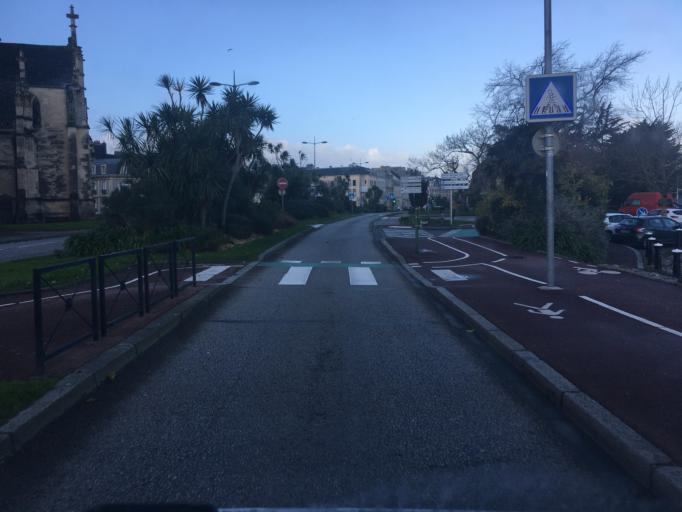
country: FR
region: Lower Normandy
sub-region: Departement de la Manche
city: Cherbourg-Octeville
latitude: 49.6423
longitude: -1.6223
